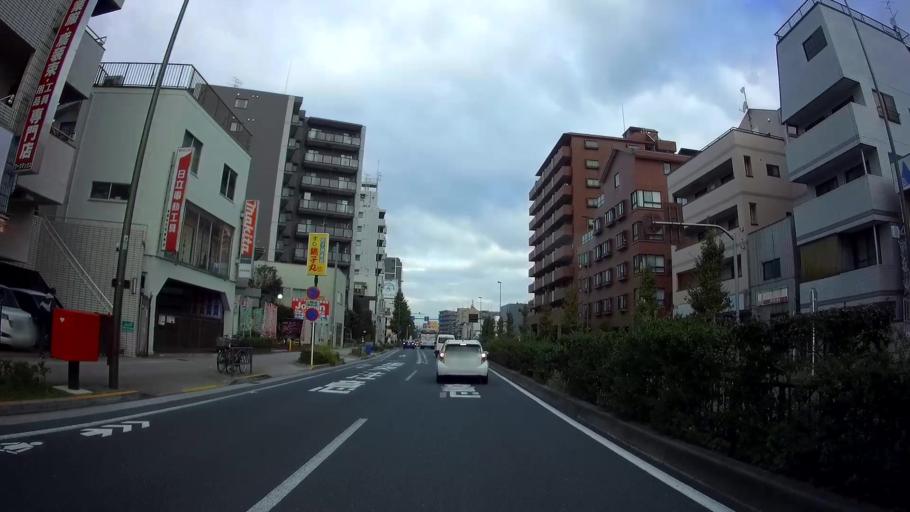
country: JP
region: Saitama
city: Shimotoda
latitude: 35.7581
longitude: 139.6831
